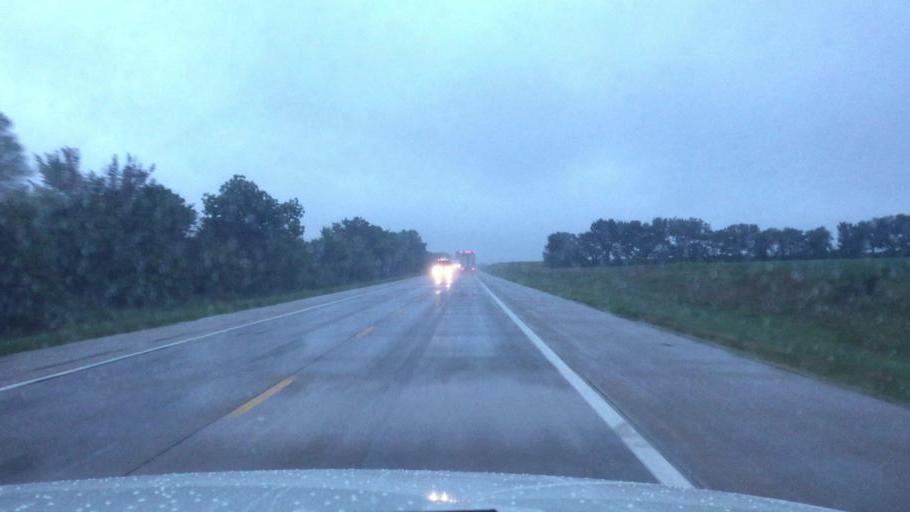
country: US
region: Kansas
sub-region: Neosho County
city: Chanute
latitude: 37.5427
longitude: -95.4708
